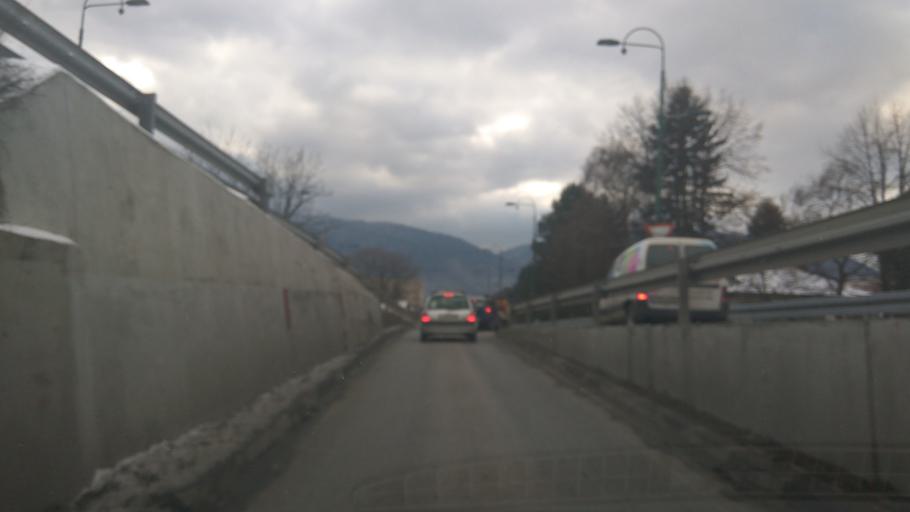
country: BA
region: Federation of Bosnia and Herzegovina
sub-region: Kanton Sarajevo
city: Sarajevo
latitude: 43.8339
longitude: 18.3093
